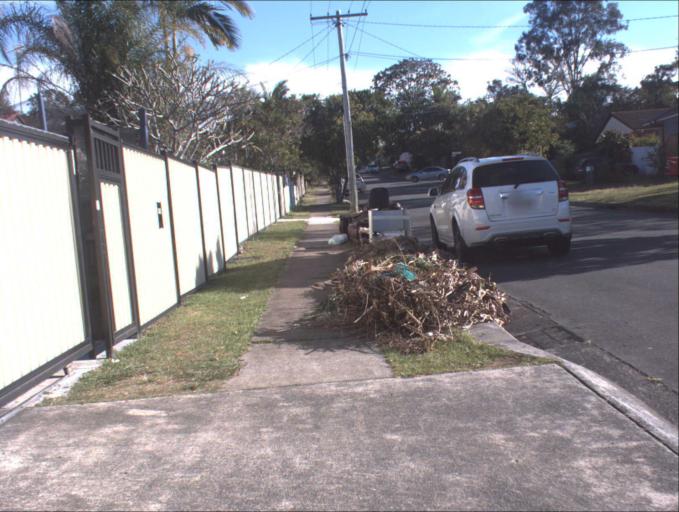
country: AU
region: Queensland
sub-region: Logan
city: Slacks Creek
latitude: -27.6474
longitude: 153.1322
